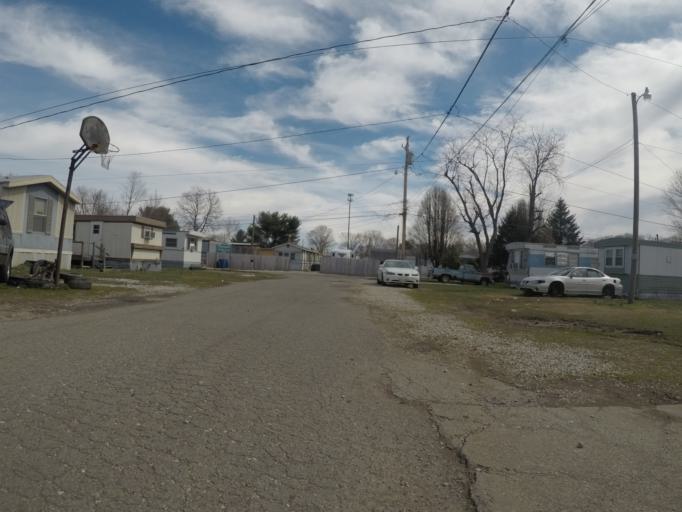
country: US
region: West Virginia
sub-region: Cabell County
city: Pea Ridge
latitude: 38.4169
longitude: -82.3521
